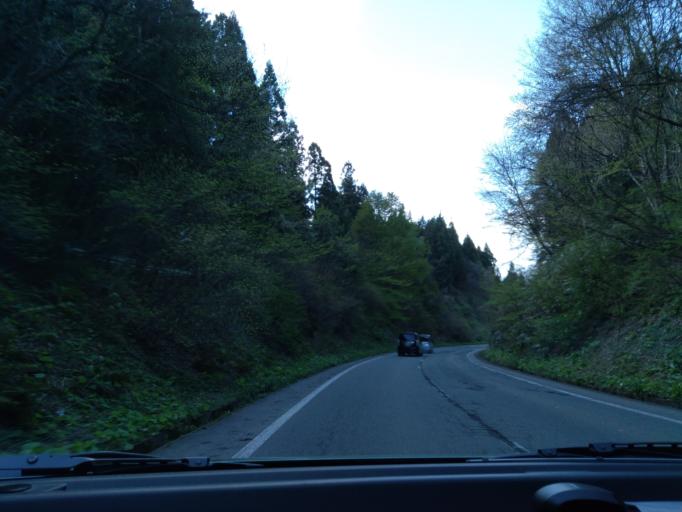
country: JP
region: Akita
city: Akita
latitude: 39.6899
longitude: 140.2751
